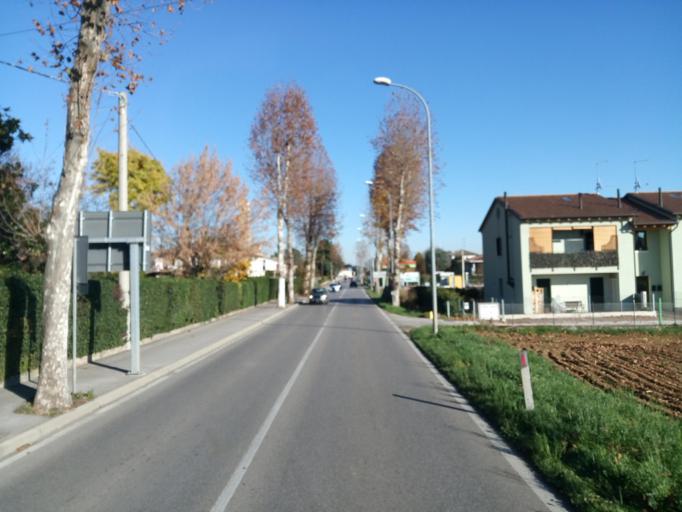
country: IT
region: Veneto
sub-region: Provincia di Treviso
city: Selva del Montello
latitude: 45.7840
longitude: 12.1379
